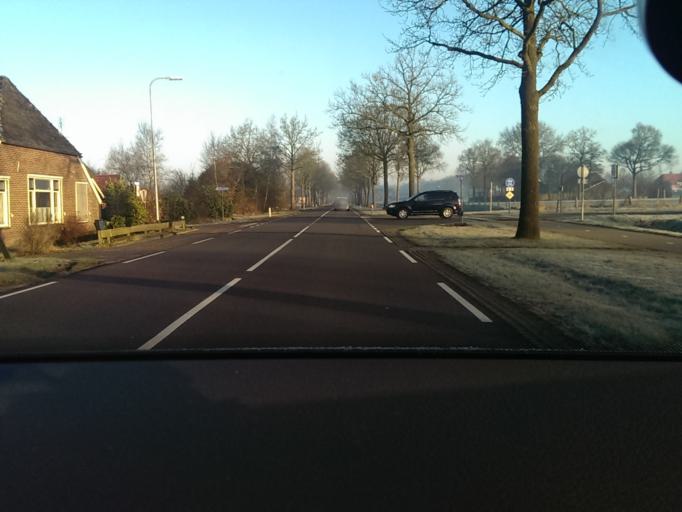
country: NL
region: Overijssel
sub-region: Gemeente Twenterand
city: Vroomshoop
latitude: 52.4224
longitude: 6.5486
